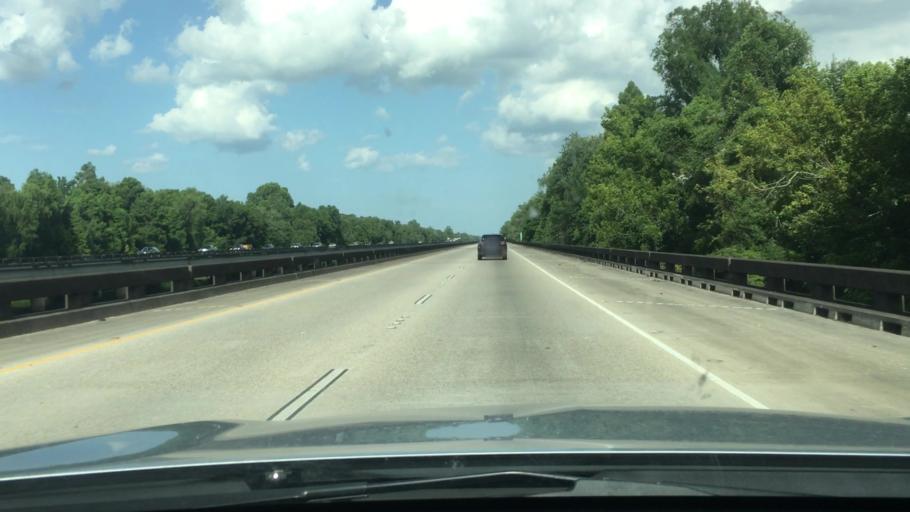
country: US
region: Louisiana
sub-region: Saint John the Baptist Parish
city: Reserve
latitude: 30.1122
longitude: -90.5602
